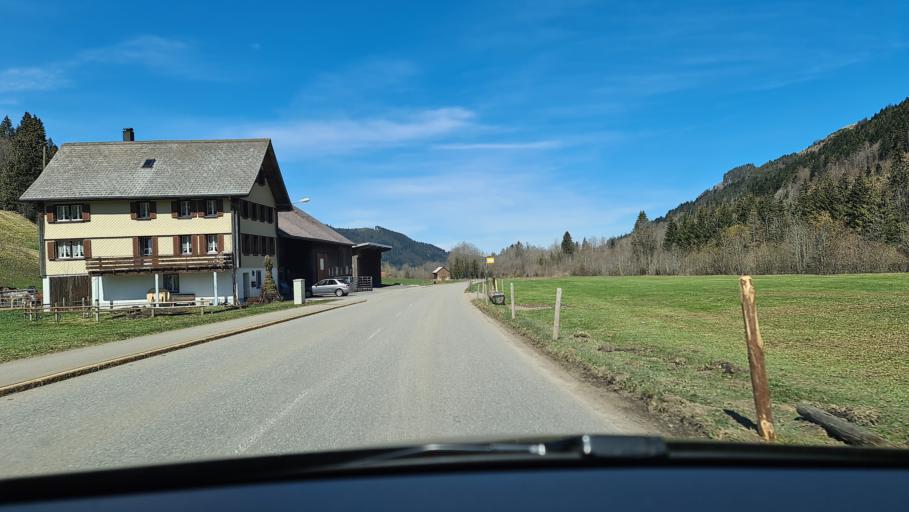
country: CH
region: Schwyz
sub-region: Bezirk Schwyz
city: Rothenthurm
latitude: 47.0782
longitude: 8.7227
